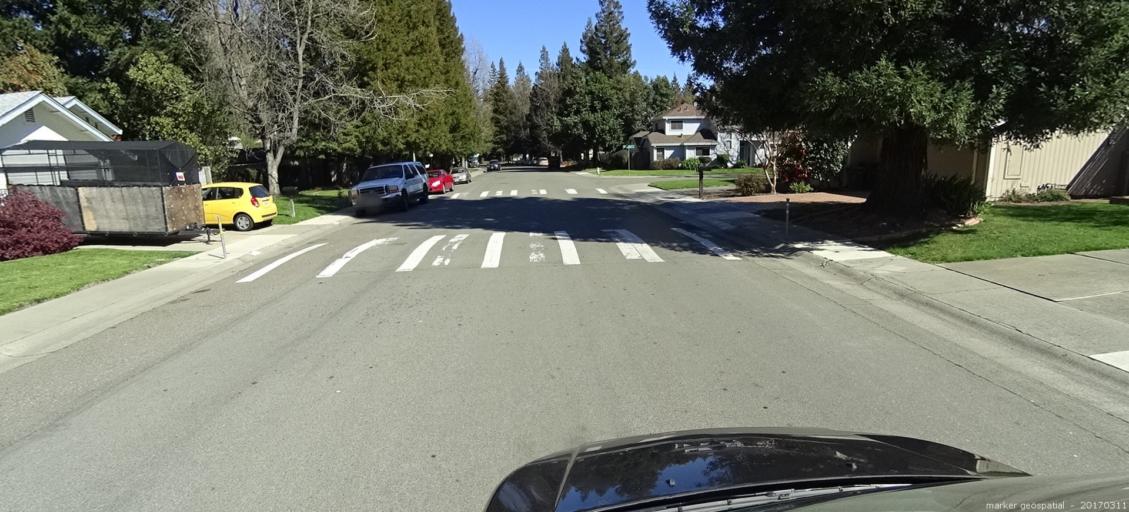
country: US
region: California
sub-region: Yolo County
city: West Sacramento
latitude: 38.4960
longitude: -121.5454
